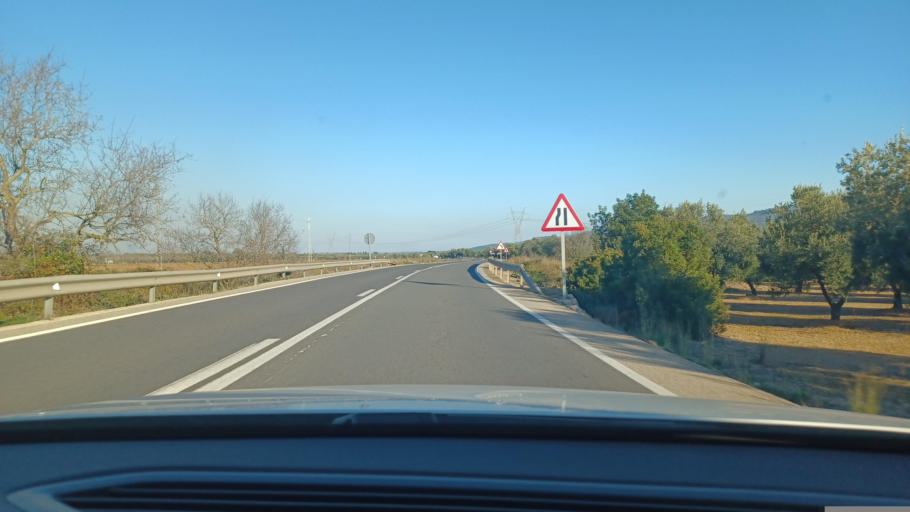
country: ES
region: Catalonia
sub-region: Provincia de Tarragona
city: Ulldecona
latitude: 40.6673
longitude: 0.4341
